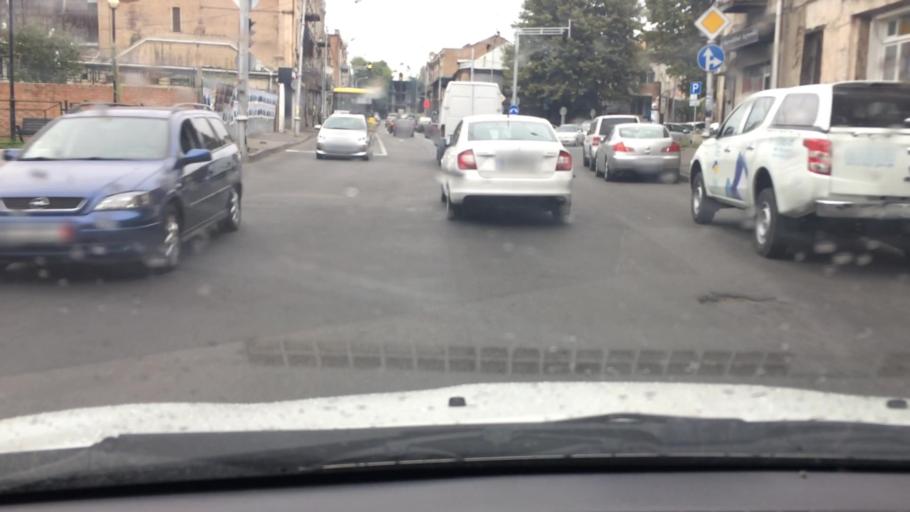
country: GE
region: T'bilisi
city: Tbilisi
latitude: 41.7025
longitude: 44.8070
